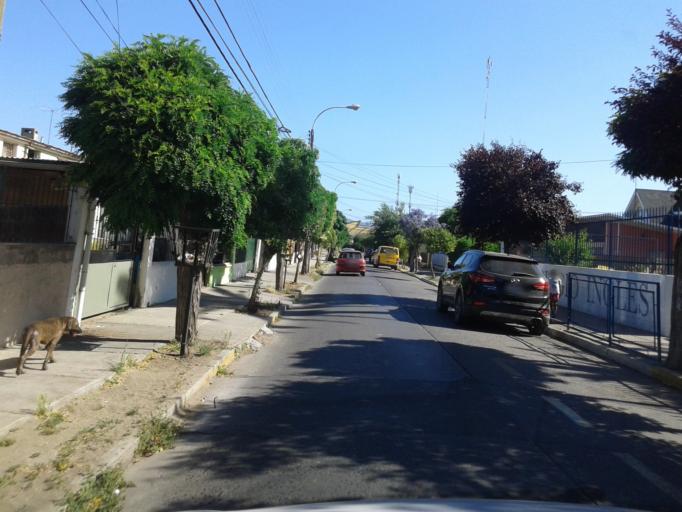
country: CL
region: Valparaiso
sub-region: Provincia de Quillota
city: Quillota
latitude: -32.8829
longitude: -71.2509
